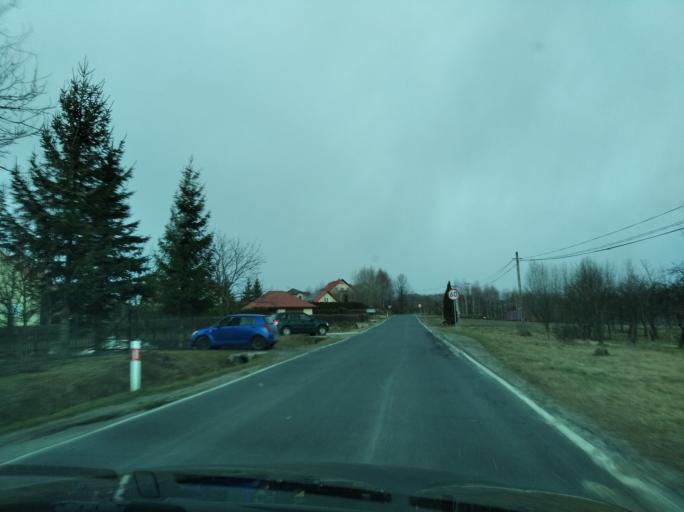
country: PL
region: Subcarpathian Voivodeship
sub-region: Powiat rzeszowski
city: Hyzne
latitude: 49.9151
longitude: 22.1988
